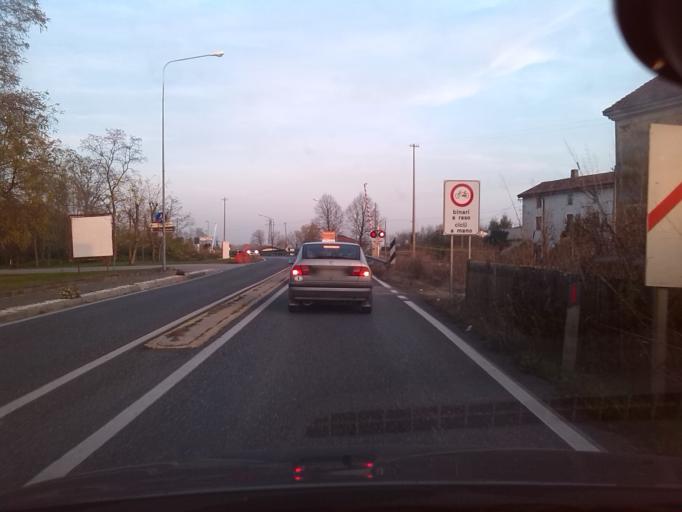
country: IT
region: Friuli Venezia Giulia
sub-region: Provincia di Udine
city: Remanzacco
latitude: 46.0859
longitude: 13.3334
